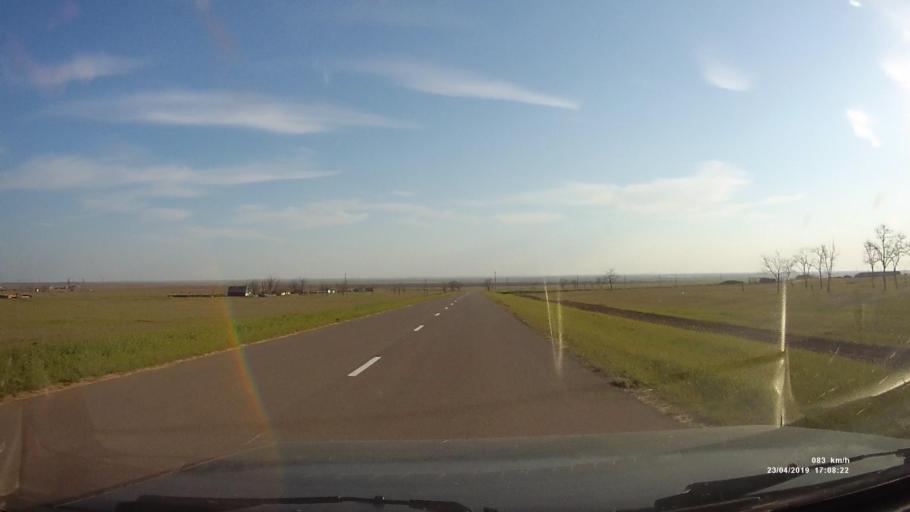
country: RU
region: Kalmykiya
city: Priyutnoye
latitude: 46.2719
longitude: 43.4887
